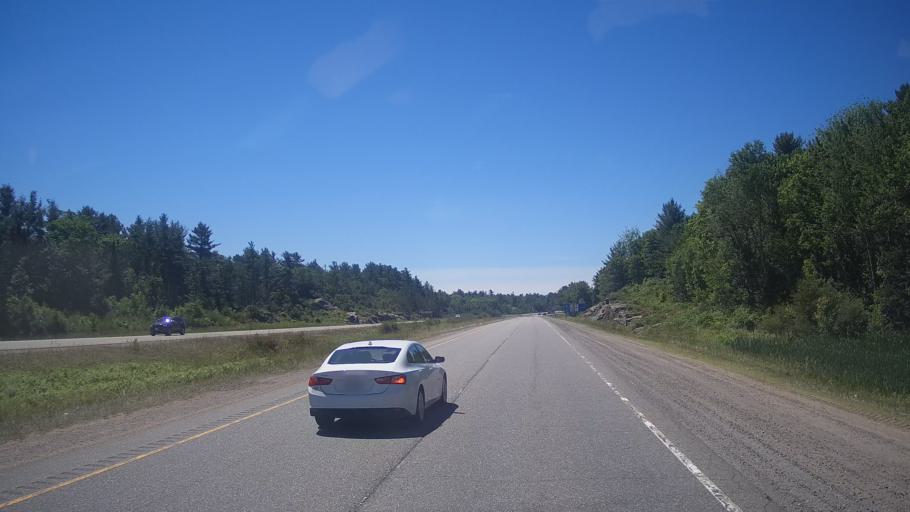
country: CA
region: Ontario
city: Gravenhurst
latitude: 44.9241
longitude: -79.3436
